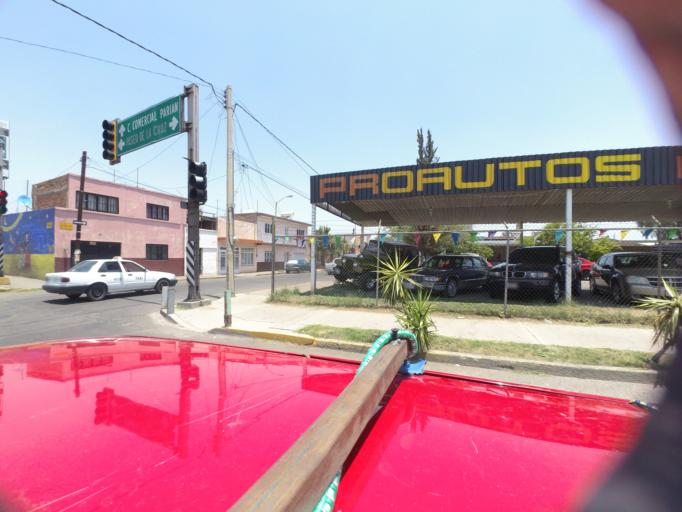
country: MX
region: Aguascalientes
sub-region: Aguascalientes
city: Aguascalientes
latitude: 21.8723
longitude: -102.2930
